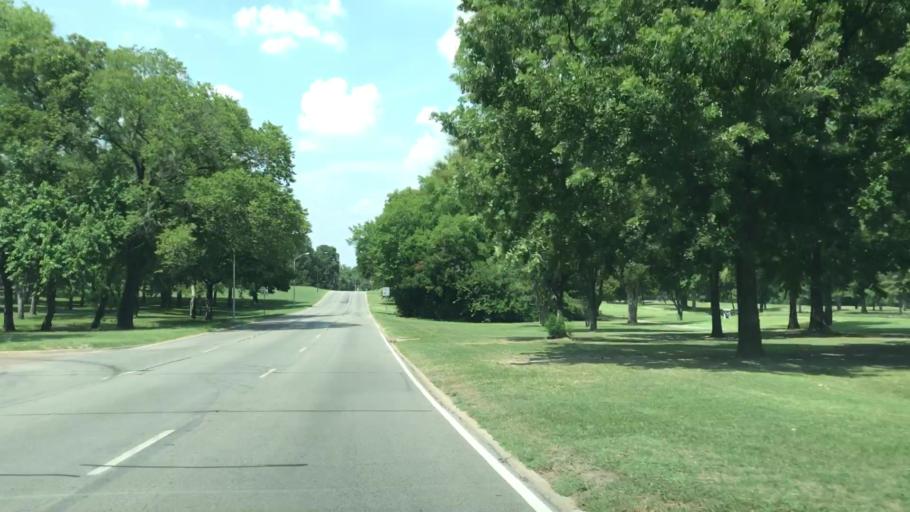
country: US
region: Texas
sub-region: Dallas County
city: Highland Park
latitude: 32.8012
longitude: -96.7367
